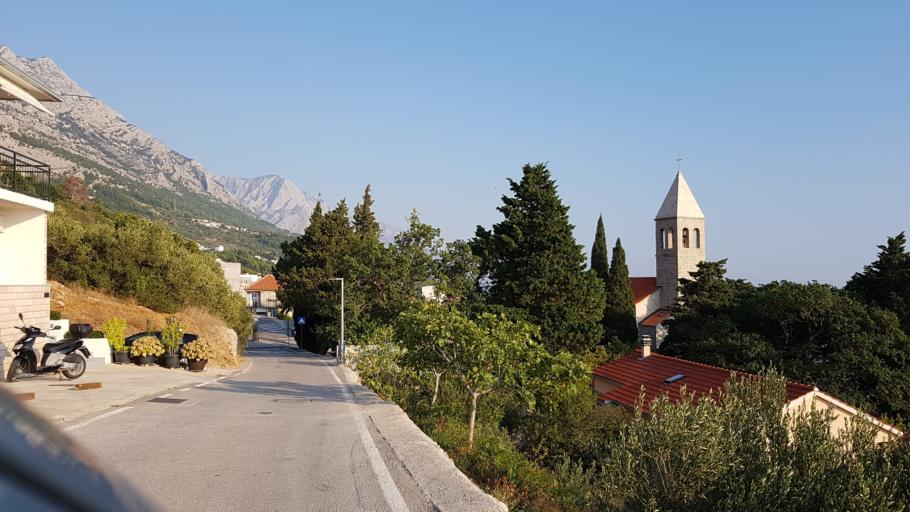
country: HR
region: Splitsko-Dalmatinska
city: Donja Brela
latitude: 43.3847
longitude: 16.9072
